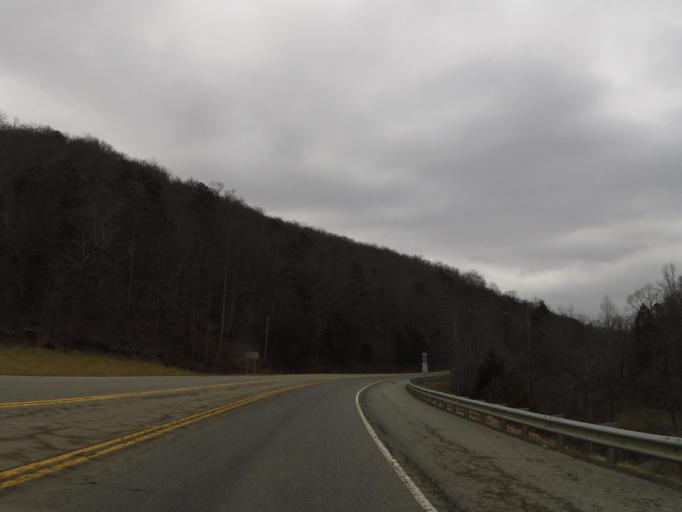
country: US
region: Tennessee
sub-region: Campbell County
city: Caryville
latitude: 36.4147
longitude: -84.3008
